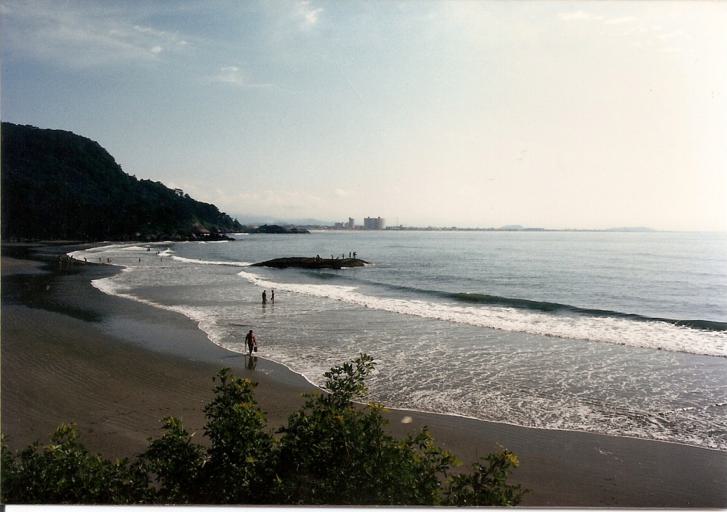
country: BR
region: Sao Paulo
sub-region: Peruibe
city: Peruibe
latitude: -24.3510
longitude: -46.9992
